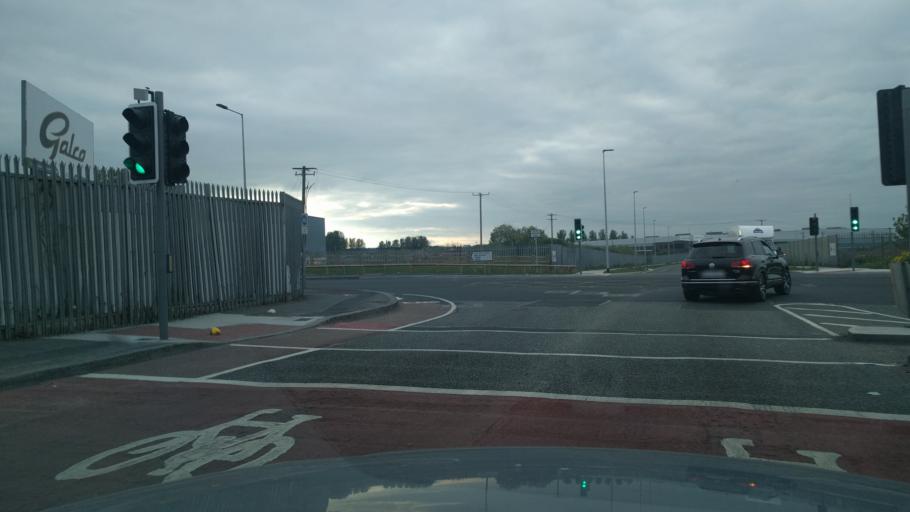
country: IE
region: Leinster
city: Crumlin
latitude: 53.3151
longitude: -6.3513
